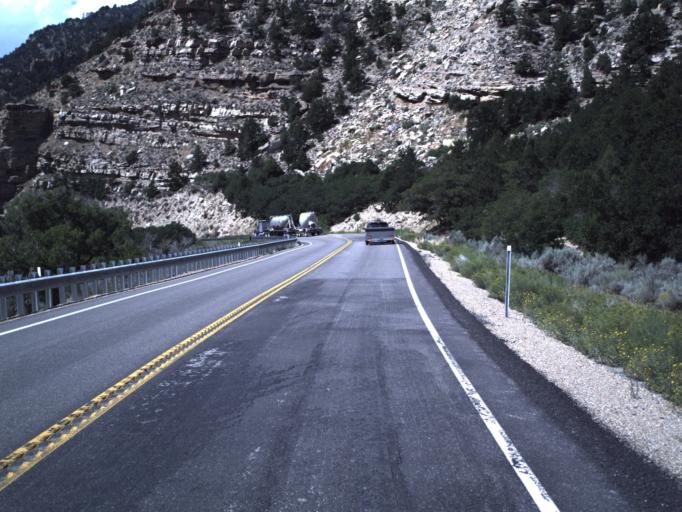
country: US
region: Utah
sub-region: Carbon County
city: Helper
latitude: 39.7500
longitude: -110.8292
